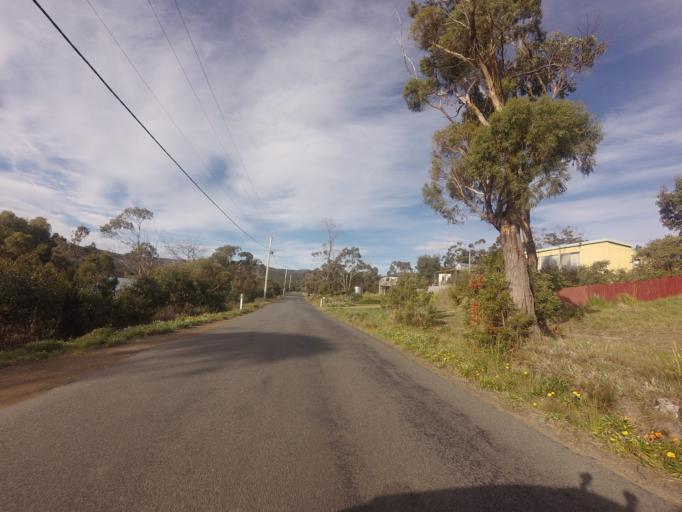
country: AU
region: Tasmania
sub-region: Sorell
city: Sorell
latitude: -42.9462
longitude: 147.8555
